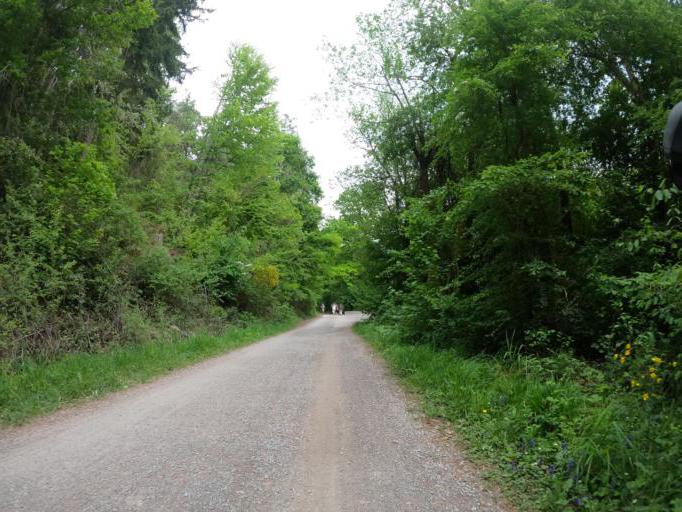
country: DE
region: Baden-Wuerttemberg
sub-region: Tuebingen Region
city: Dettenhausen
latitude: 48.6028
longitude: 9.1150
